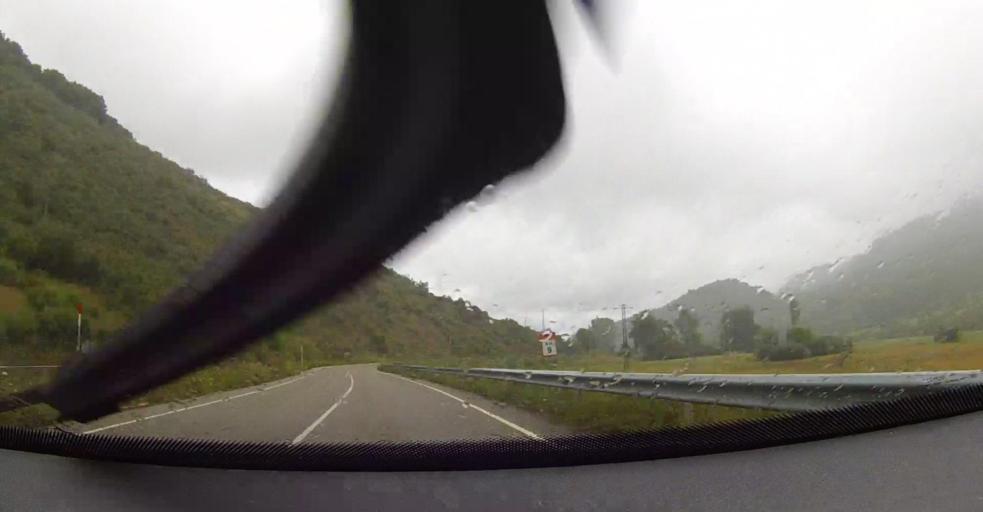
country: ES
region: Castille and Leon
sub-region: Provincia de Leon
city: Acebedo
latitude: 43.0407
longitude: -5.1082
